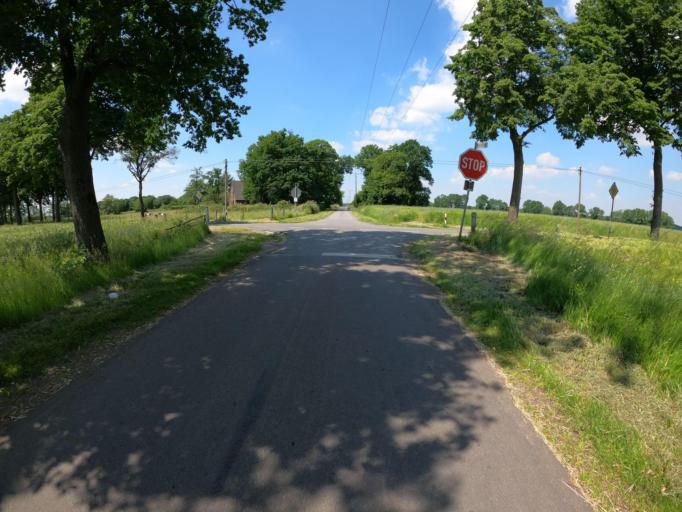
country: DE
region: North Rhine-Westphalia
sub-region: Regierungsbezirk Dusseldorf
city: Hunxe
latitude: 51.7056
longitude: 6.7471
